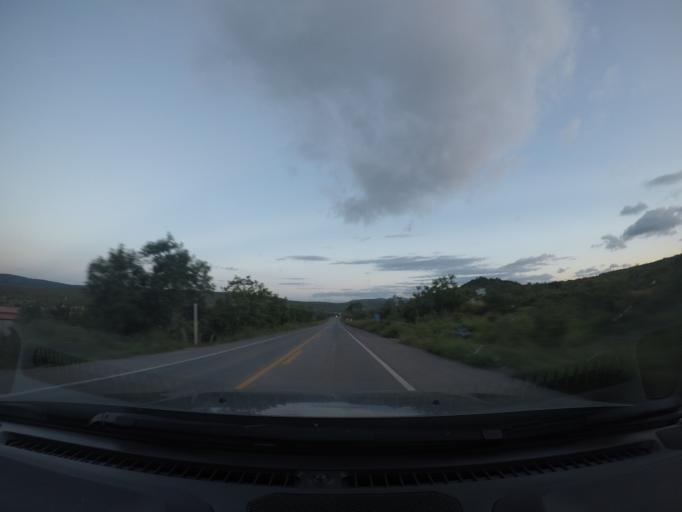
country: BR
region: Bahia
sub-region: Seabra
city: Seabra
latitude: -12.4279
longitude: -41.7612
